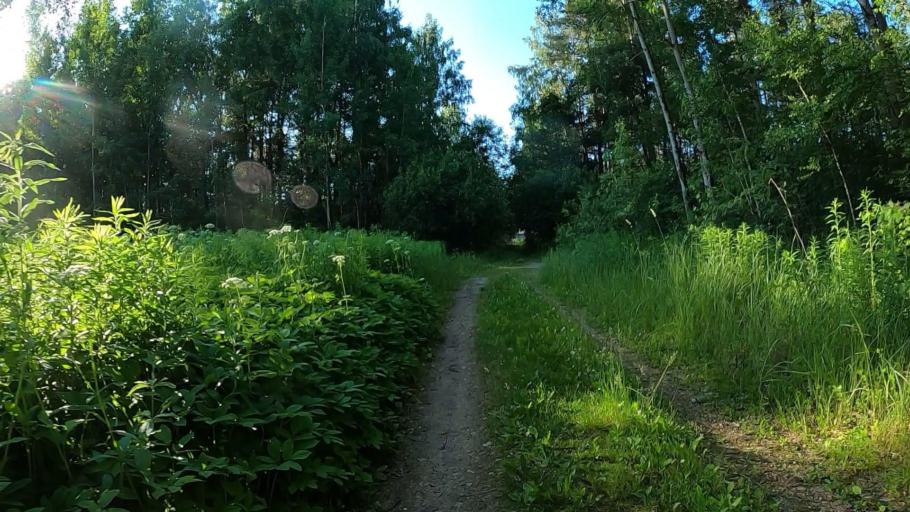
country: LV
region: Stopini
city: Ulbroka
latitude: 56.9294
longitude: 24.2334
